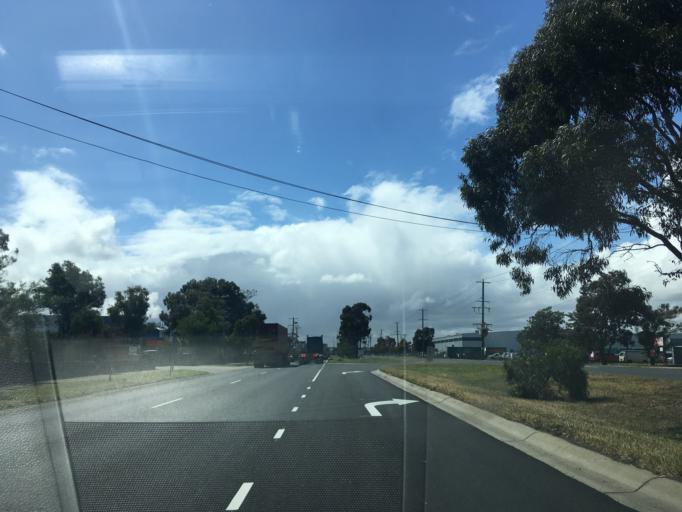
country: AU
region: Victoria
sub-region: Brimbank
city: Derrimut
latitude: -37.8177
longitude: 144.7868
